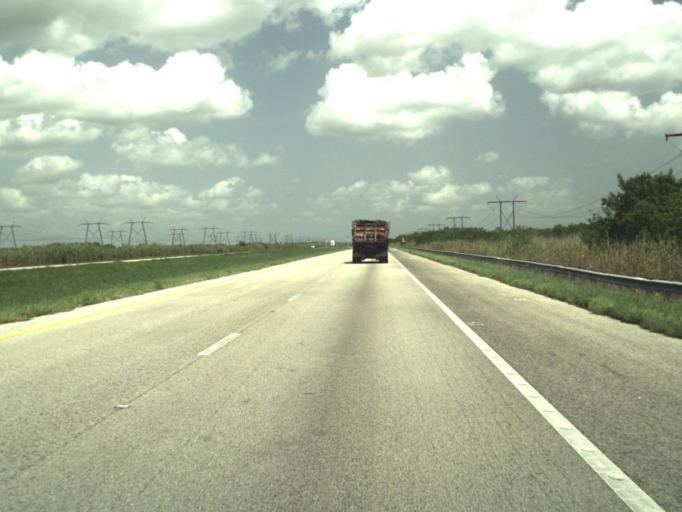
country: US
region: Florida
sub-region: Broward County
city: Weston
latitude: 26.2611
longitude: -80.4807
